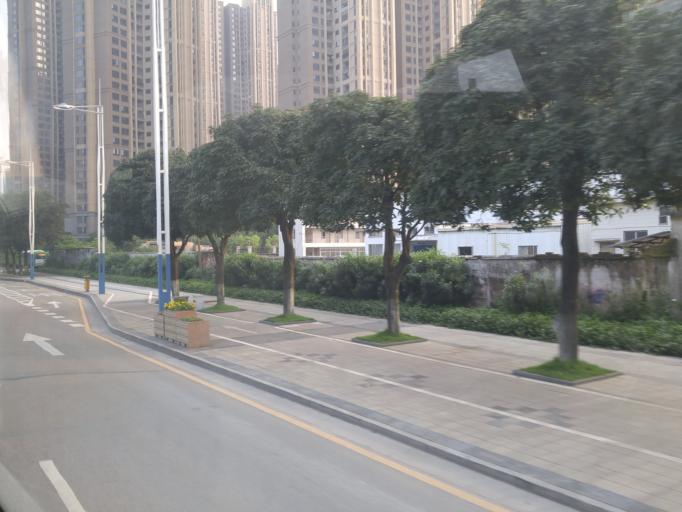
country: CN
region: Guangdong
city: Foshan
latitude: 23.0692
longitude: 113.1405
